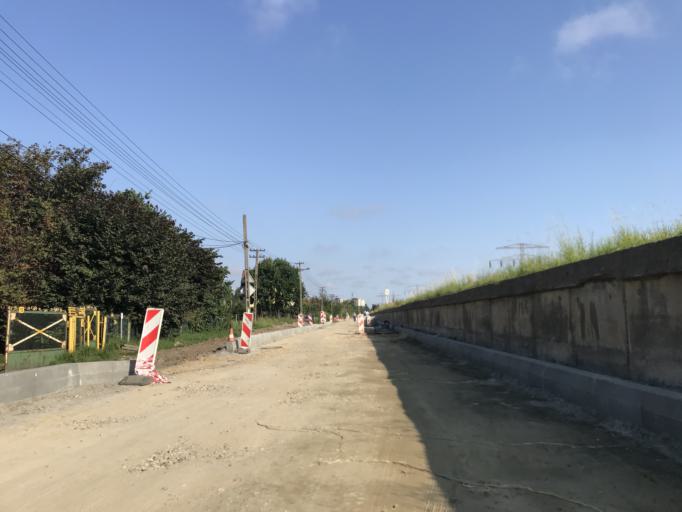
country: PL
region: Pomeranian Voivodeship
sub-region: Gdansk
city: Gdansk
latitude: 54.3428
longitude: 18.6832
